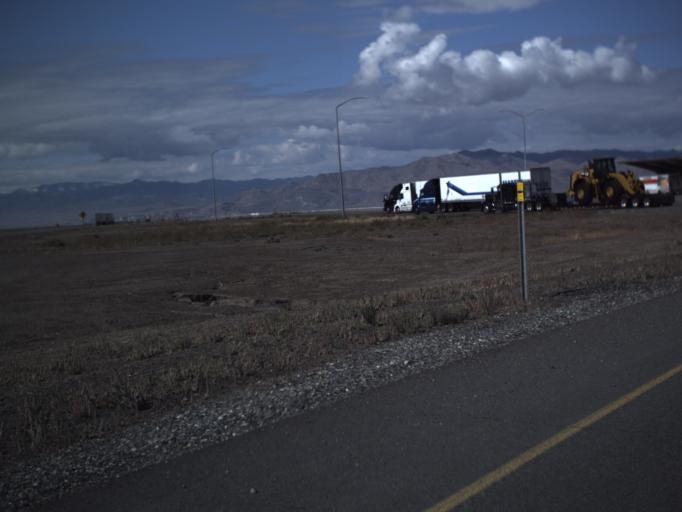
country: US
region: Utah
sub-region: Tooele County
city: Wendover
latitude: 40.7397
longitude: -113.8505
